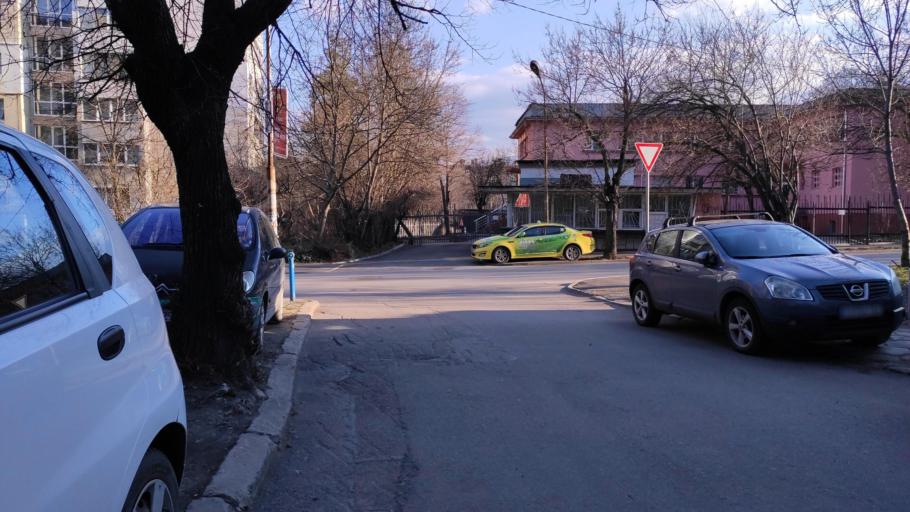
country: BG
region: Sofia-Capital
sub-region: Stolichna Obshtina
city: Sofia
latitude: 42.7080
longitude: 23.2803
